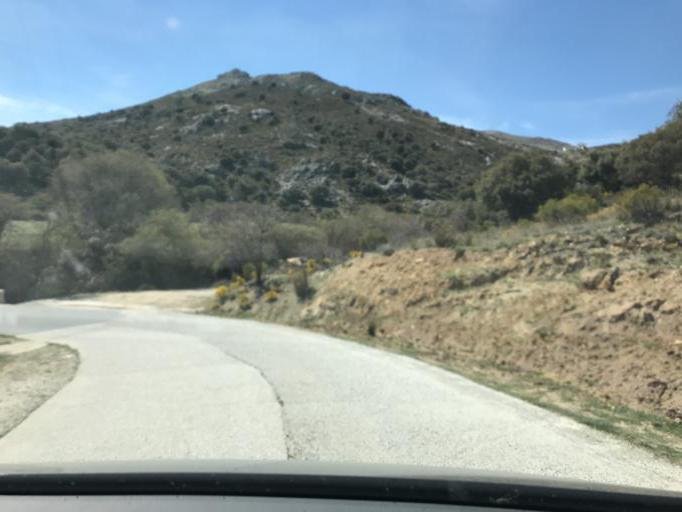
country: ES
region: Andalusia
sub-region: Provincia de Granada
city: Iznalloz
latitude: 37.3199
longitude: -3.4593
